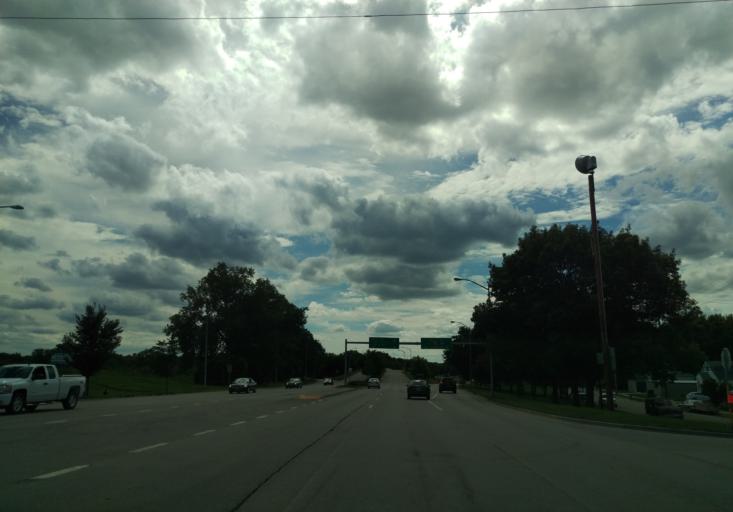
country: US
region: Wisconsin
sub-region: Dane County
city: Maple Bluff
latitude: 43.1163
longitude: -89.3550
